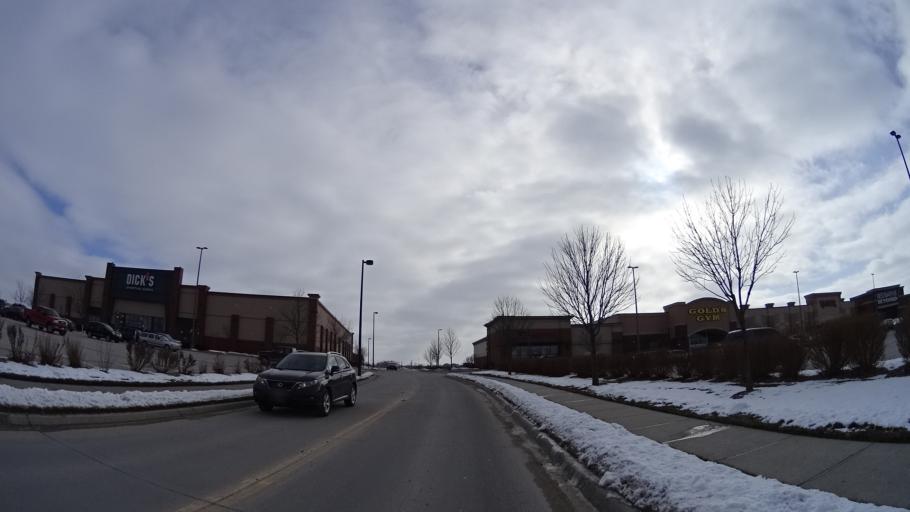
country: US
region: Nebraska
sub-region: Sarpy County
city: Papillion
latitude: 41.1340
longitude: -96.0274
